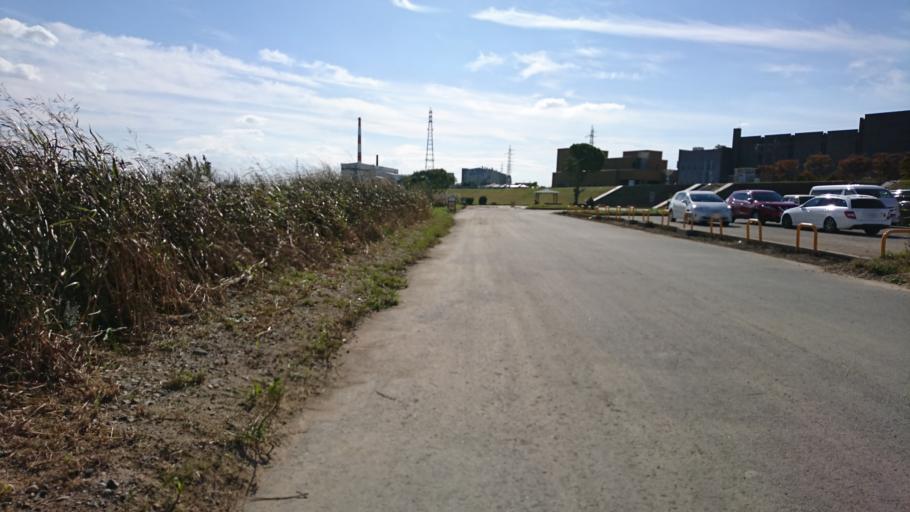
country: JP
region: Hyogo
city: Kakogawacho-honmachi
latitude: 34.7563
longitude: 134.8058
